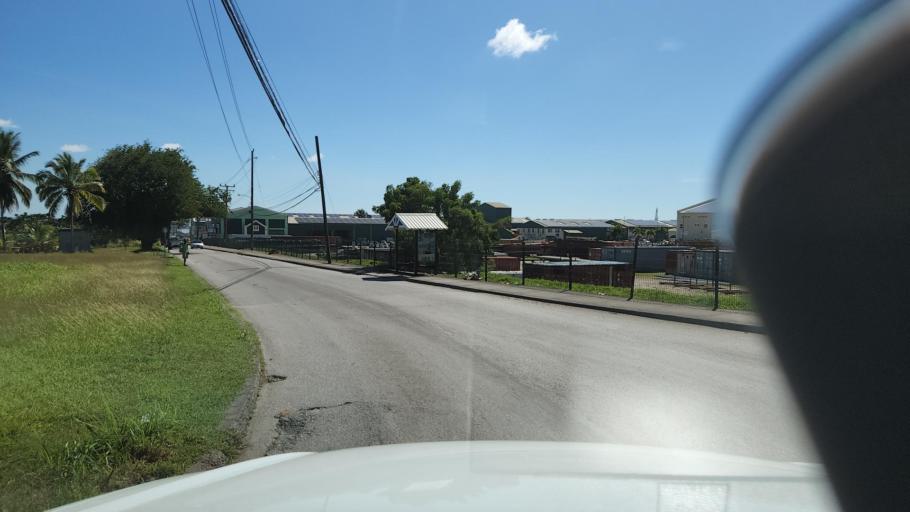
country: BB
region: Saint Thomas
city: Welchman Hall
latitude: 13.1580
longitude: -59.6013
